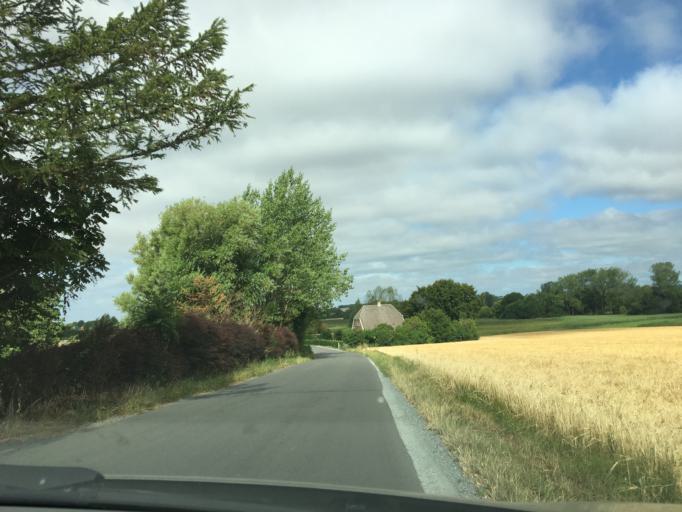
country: DK
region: South Denmark
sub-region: Middelfart Kommune
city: Norre Aby
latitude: 55.5060
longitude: 9.8769
